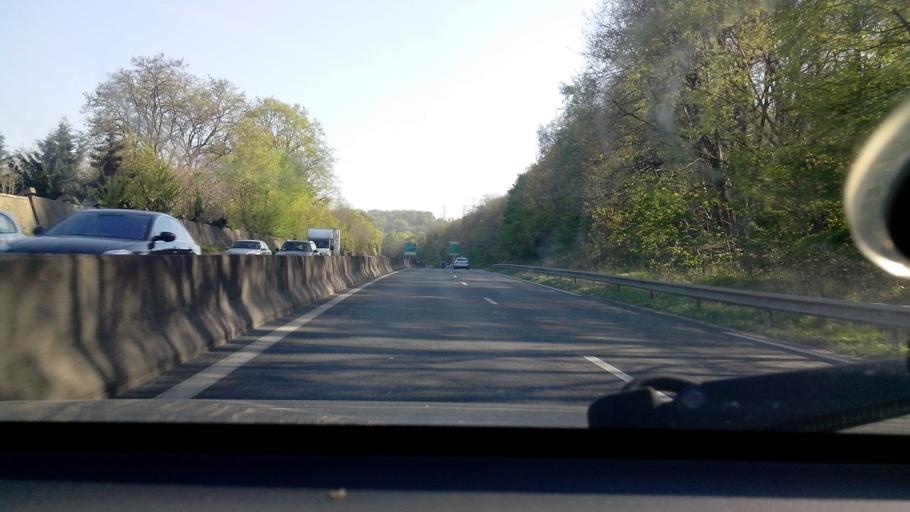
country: FR
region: Ile-de-France
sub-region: Departement de l'Essonne
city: Bievres
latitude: 48.7600
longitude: 2.2253
